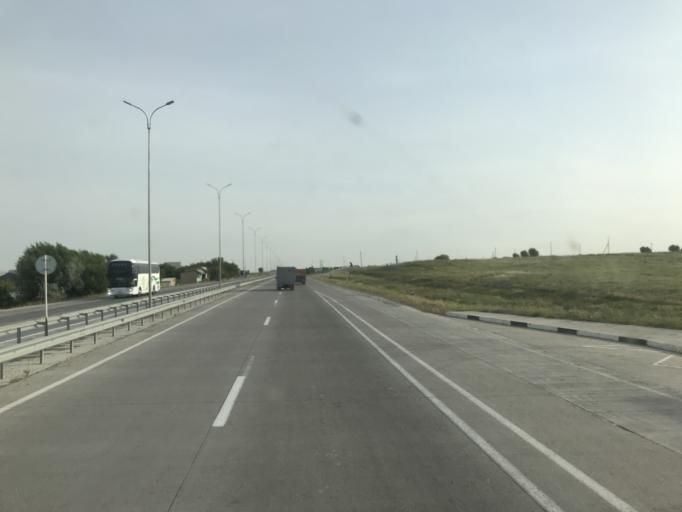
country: UZ
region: Toshkent
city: Qibray
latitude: 41.5628
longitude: 69.4083
